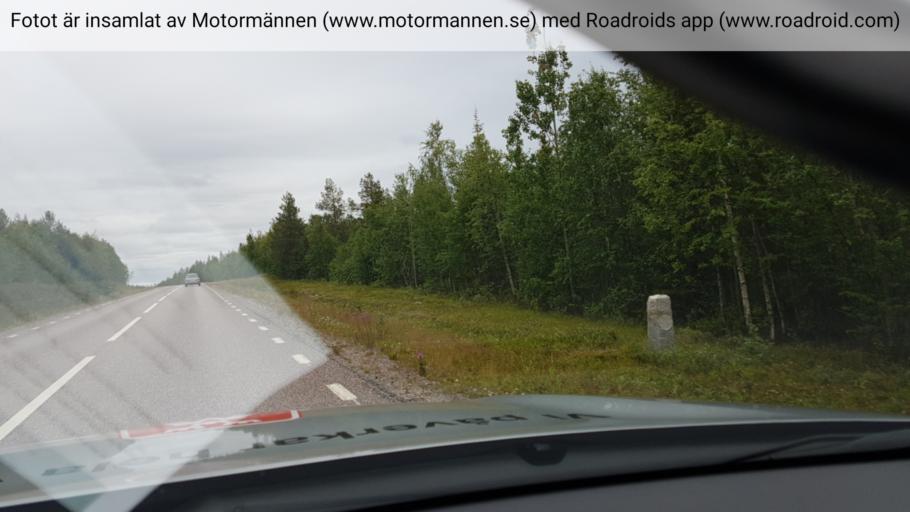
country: SE
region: Norrbotten
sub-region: Gallivare Kommun
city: Gaellivare
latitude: 67.0393
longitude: 21.6569
